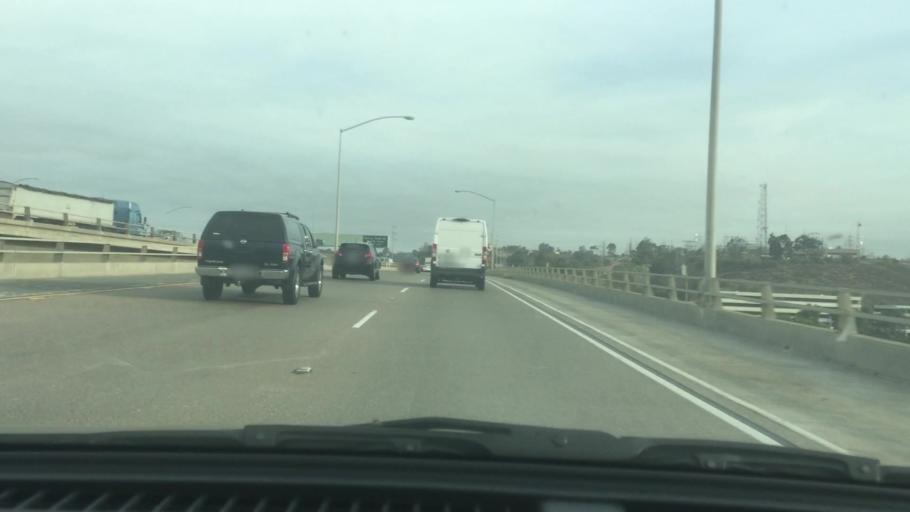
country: US
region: California
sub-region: San Diego County
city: San Diego
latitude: 32.7747
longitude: -117.1342
